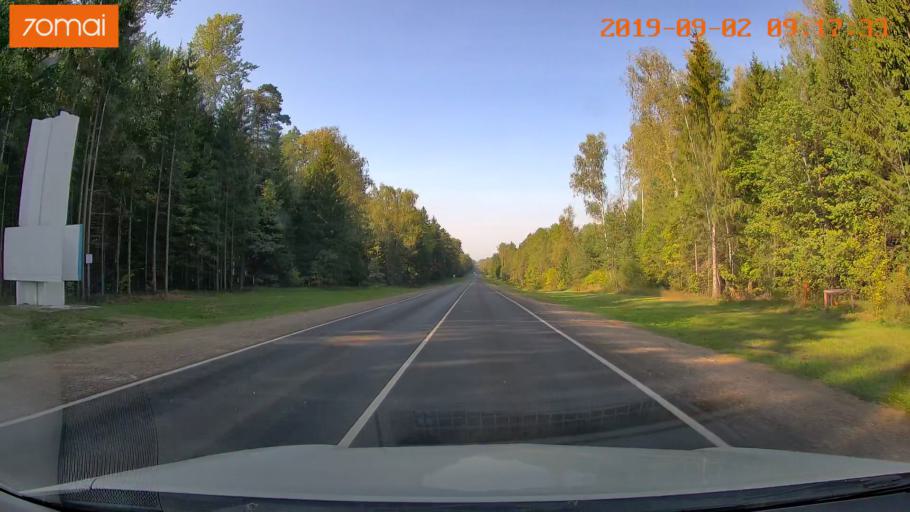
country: RU
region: Kaluga
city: Nikola-Lenivets
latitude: 54.8235
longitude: 35.4493
